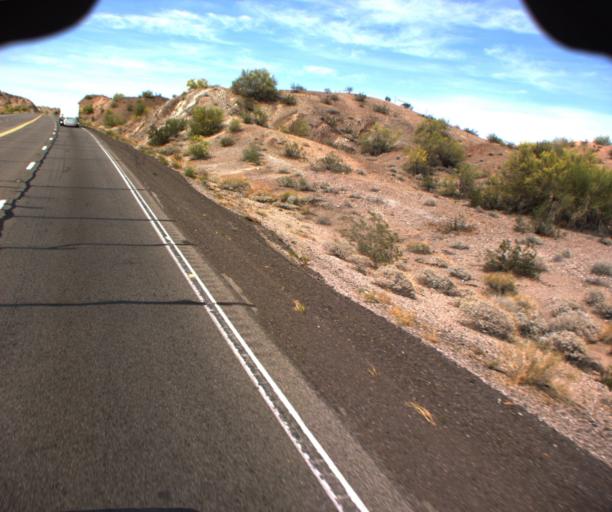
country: US
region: Arizona
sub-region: Mohave County
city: Desert Hills
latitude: 34.6354
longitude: -114.3256
